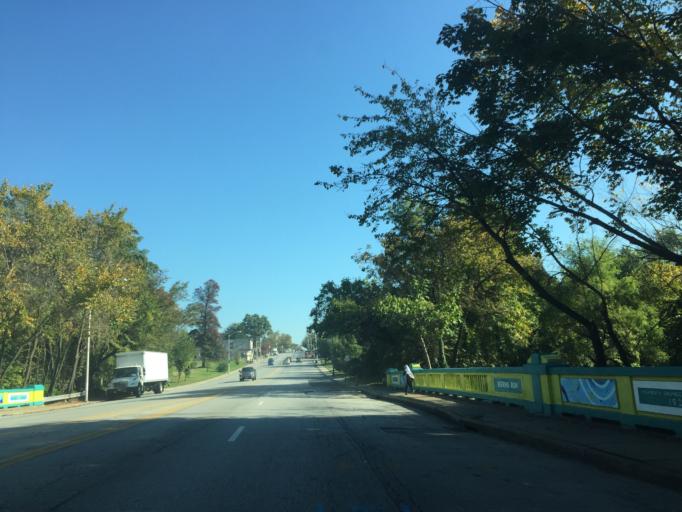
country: US
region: Maryland
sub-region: Baltimore County
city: Rosedale
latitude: 39.3261
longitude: -76.5678
